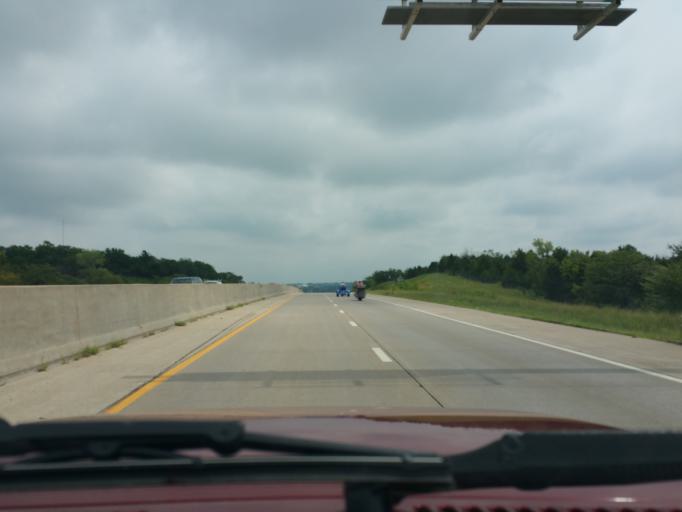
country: US
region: Kansas
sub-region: Shawnee County
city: Silver Lake
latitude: 39.0528
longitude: -95.7978
